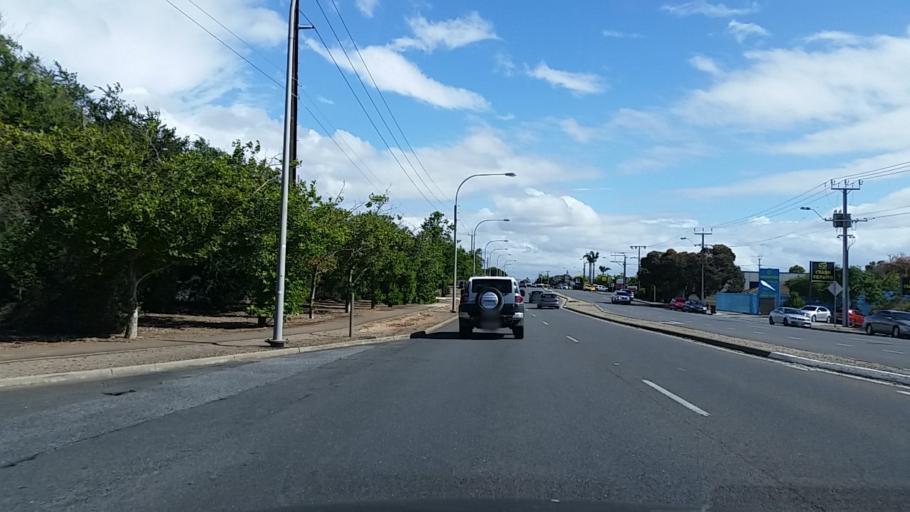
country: AU
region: South Australia
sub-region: Adelaide
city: Port Noarlunga
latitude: -35.1355
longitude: 138.4861
